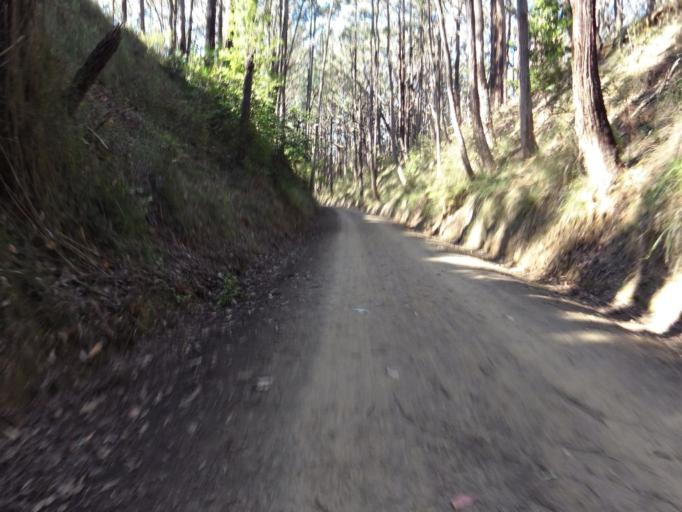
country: AU
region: Victoria
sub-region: Latrobe
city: Moe
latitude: -38.3987
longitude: 146.1742
